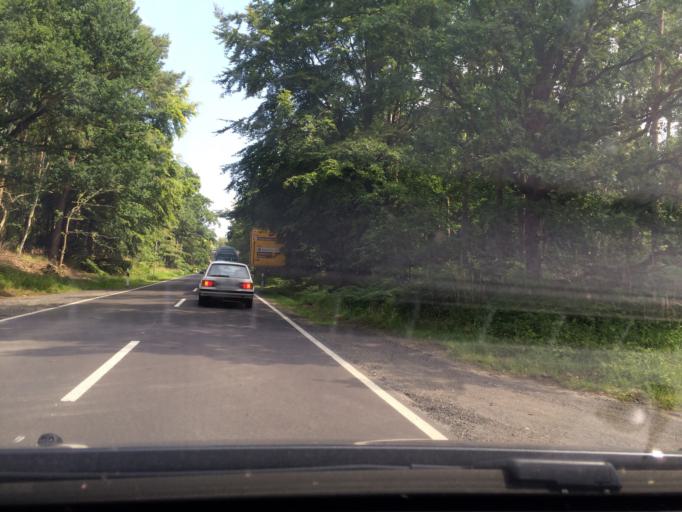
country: DE
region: Mecklenburg-Vorpommern
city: Ostseebad Binz
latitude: 54.4380
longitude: 13.5631
